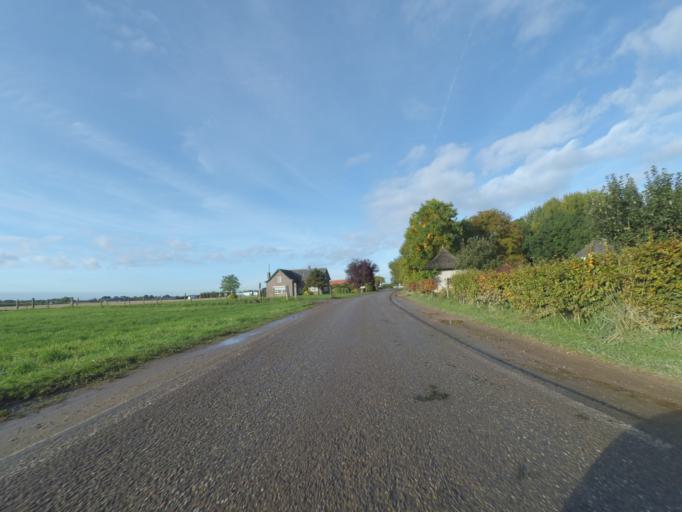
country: NL
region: Utrecht
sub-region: Gemeente Utrechtse Heuvelrug
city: Driebergen-Rijsenburg
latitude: 51.9977
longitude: 5.2730
